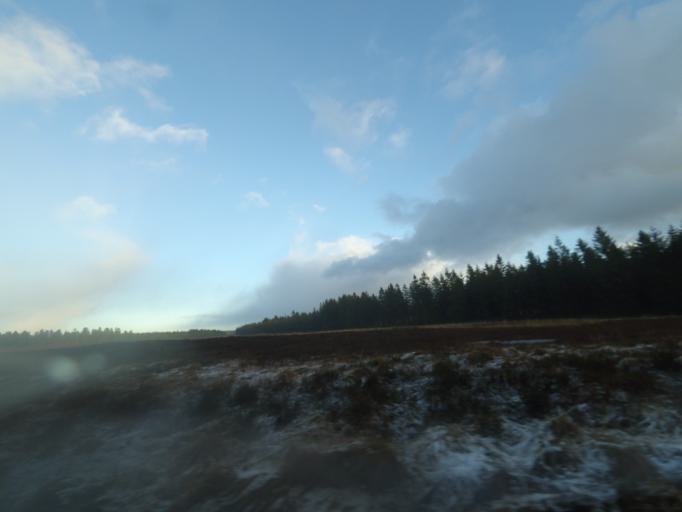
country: DK
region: Central Jutland
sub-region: Ikast-Brande Kommune
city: Brande
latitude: 56.0103
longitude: 9.1649
